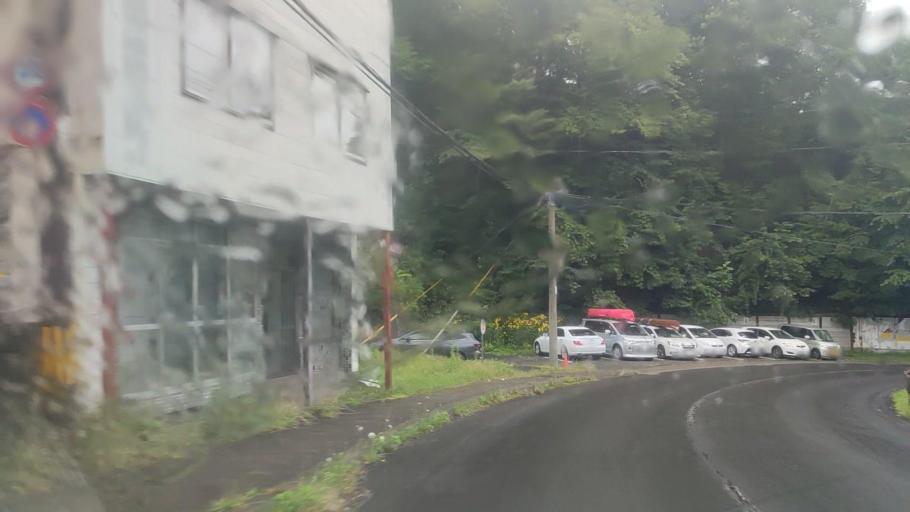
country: JP
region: Hokkaido
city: Shiraoi
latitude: 42.4909
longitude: 141.1450
